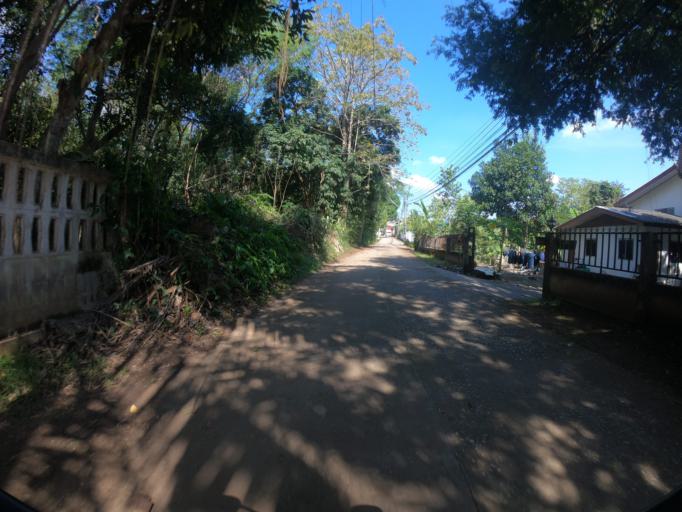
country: TH
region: Chiang Mai
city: Chiang Mai
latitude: 18.7759
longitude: 98.9499
